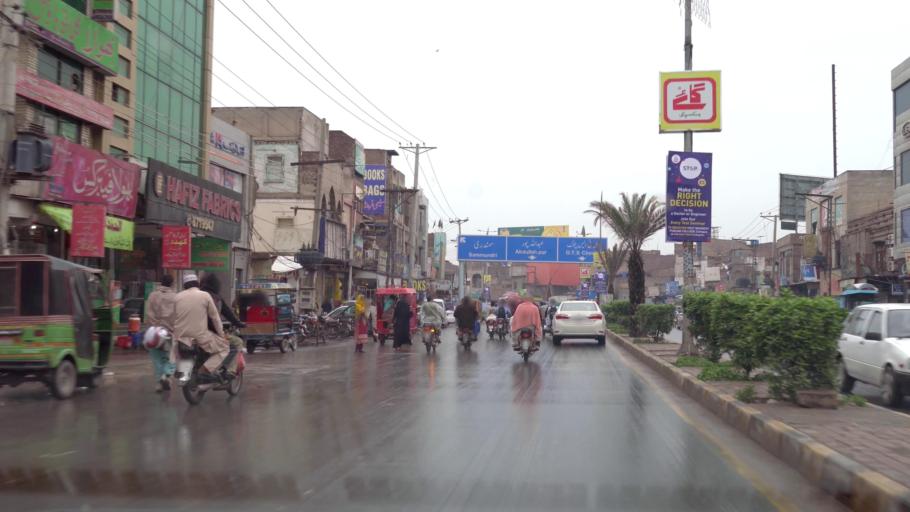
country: PK
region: Punjab
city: Faisalabad
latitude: 31.4080
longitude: 73.0984
